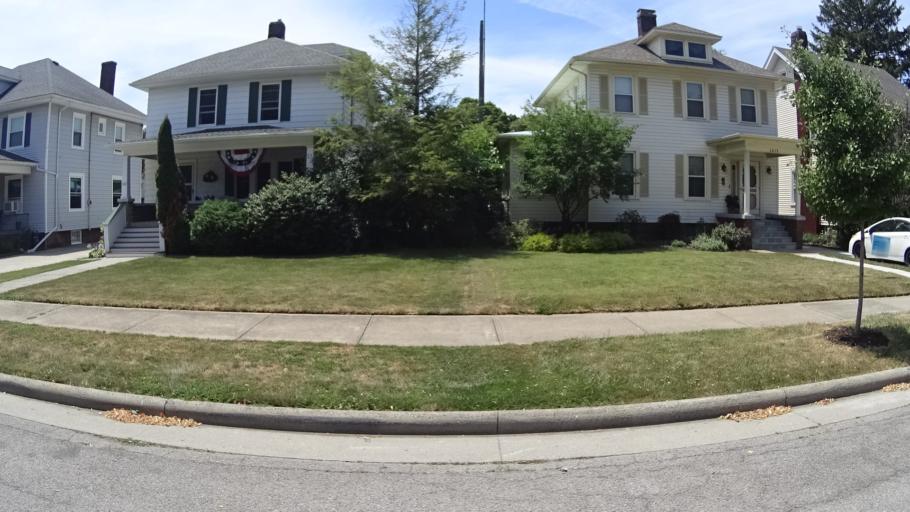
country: US
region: Ohio
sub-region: Erie County
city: Sandusky
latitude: 41.4446
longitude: -82.7030
